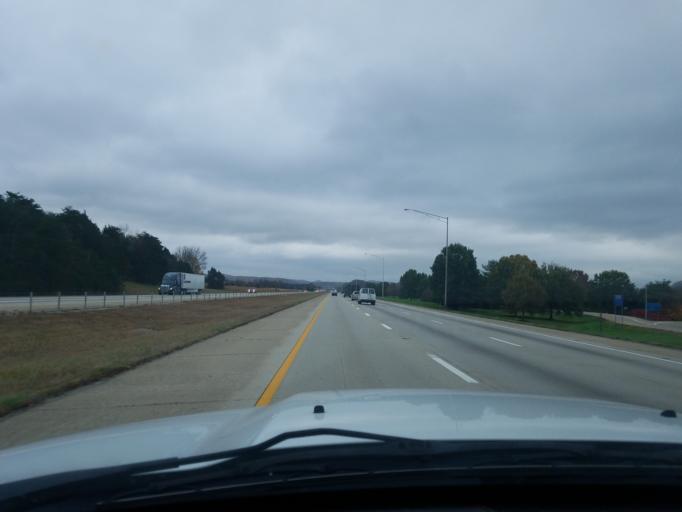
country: US
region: Kentucky
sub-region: Bullitt County
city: Shepherdsville
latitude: 37.9501
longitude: -85.6893
